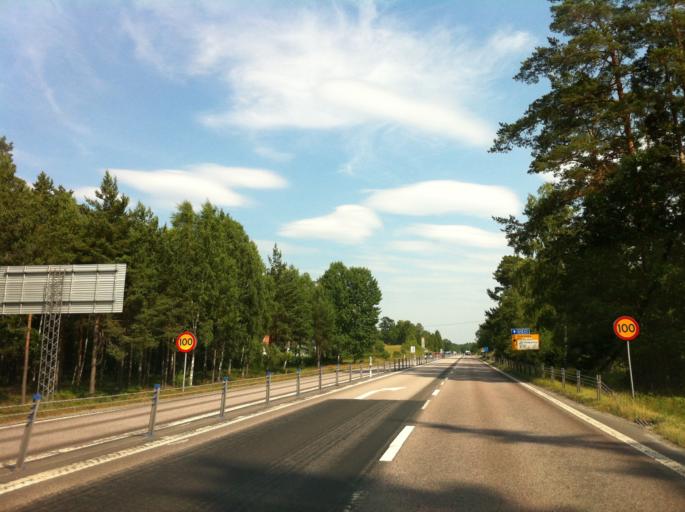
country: SE
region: Kalmar
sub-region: Nybro Kommun
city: Nybro
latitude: 56.7303
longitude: 15.9647
